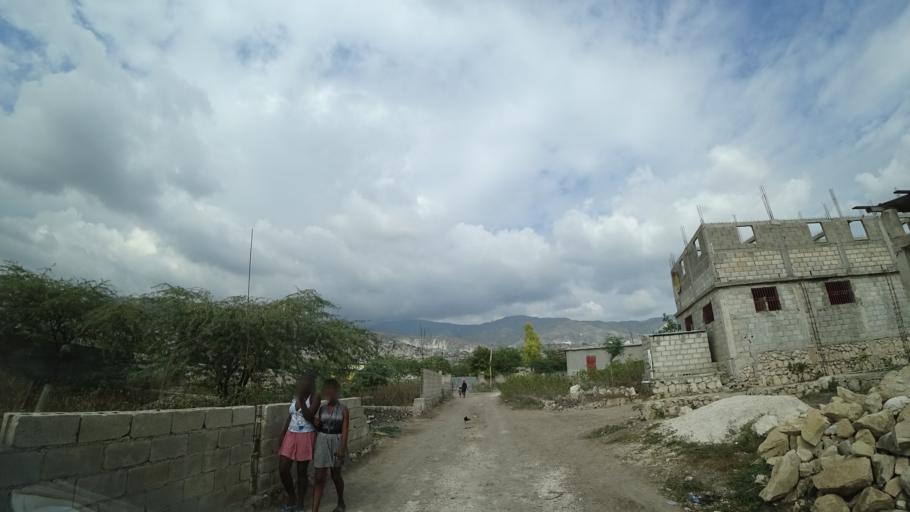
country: HT
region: Ouest
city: Croix des Bouquets
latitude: 18.6626
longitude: -72.2526
